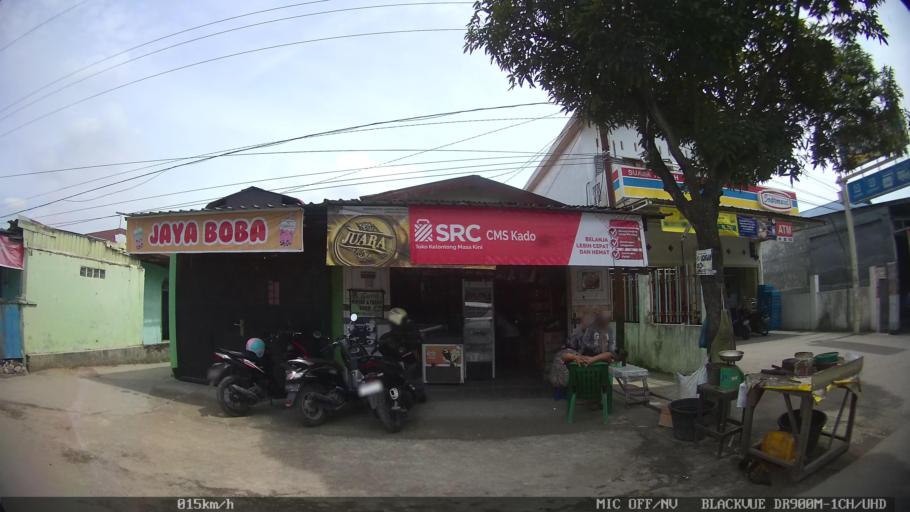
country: ID
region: North Sumatra
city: Medan
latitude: 3.6511
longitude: 98.6933
